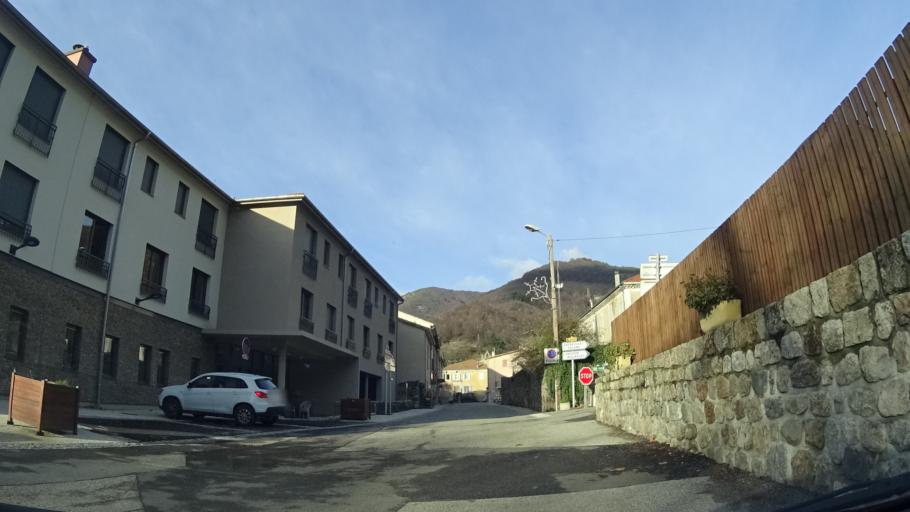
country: FR
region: Rhone-Alpes
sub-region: Departement de l'Ardeche
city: Thueyts
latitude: 44.7391
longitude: 4.2470
